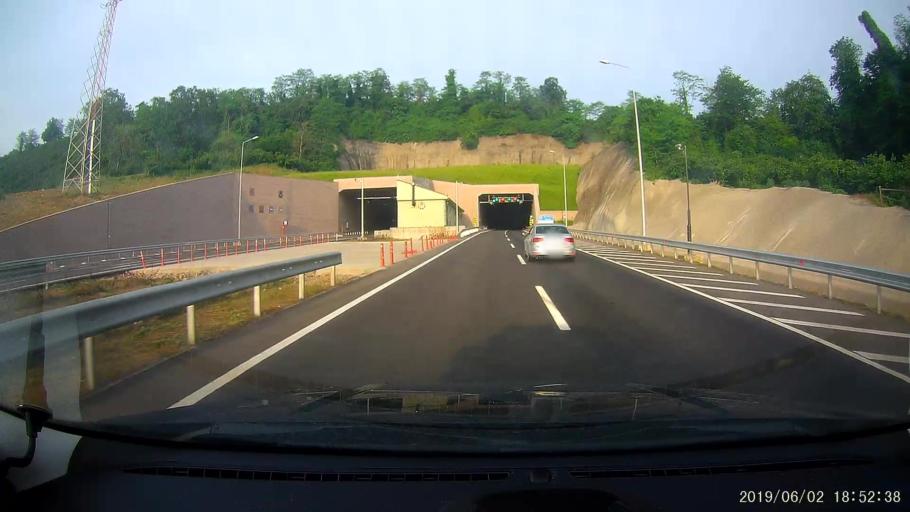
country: TR
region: Ordu
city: Ordu
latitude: 40.9881
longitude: 37.8168
